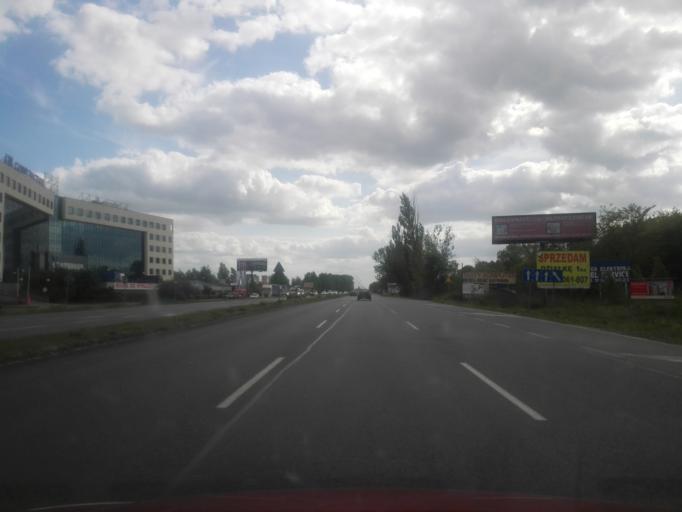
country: PL
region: Masovian Voivodeship
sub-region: Powiat wolominski
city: Zabki
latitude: 52.3015
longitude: 21.0873
